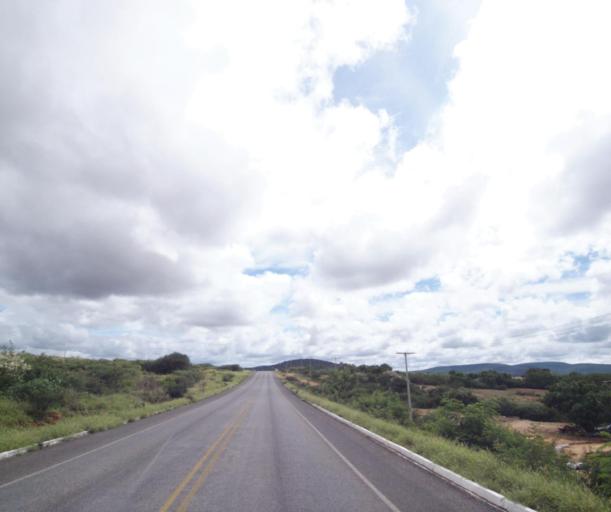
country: BR
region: Bahia
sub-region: Brumado
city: Brumado
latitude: -14.2256
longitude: -41.6736
